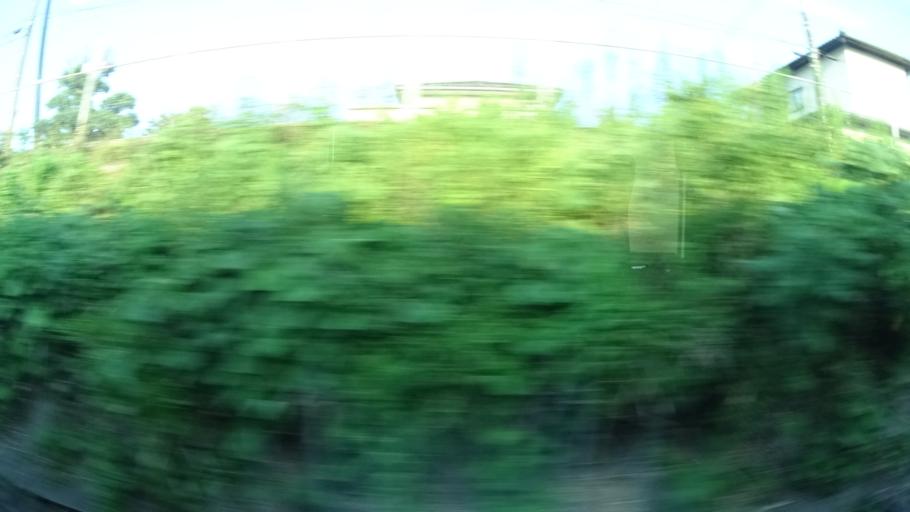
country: JP
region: Ibaraki
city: Tomobe
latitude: 36.3390
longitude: 140.2978
